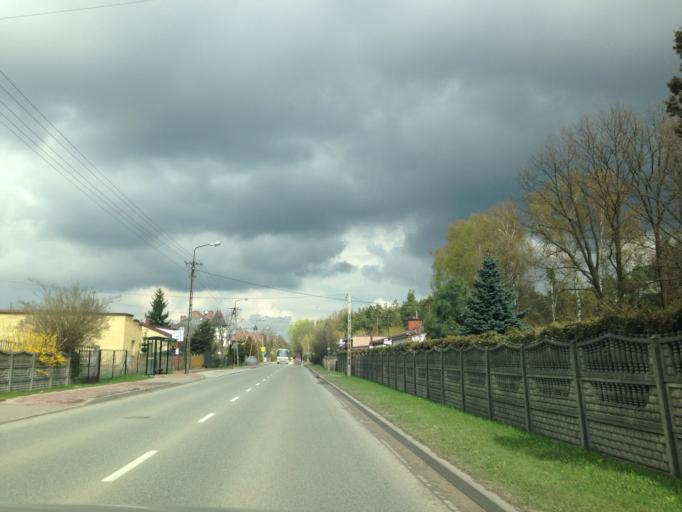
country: PL
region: Masovian Voivodeship
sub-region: Powiat warszawski zachodni
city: Babice
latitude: 52.2584
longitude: 20.8518
